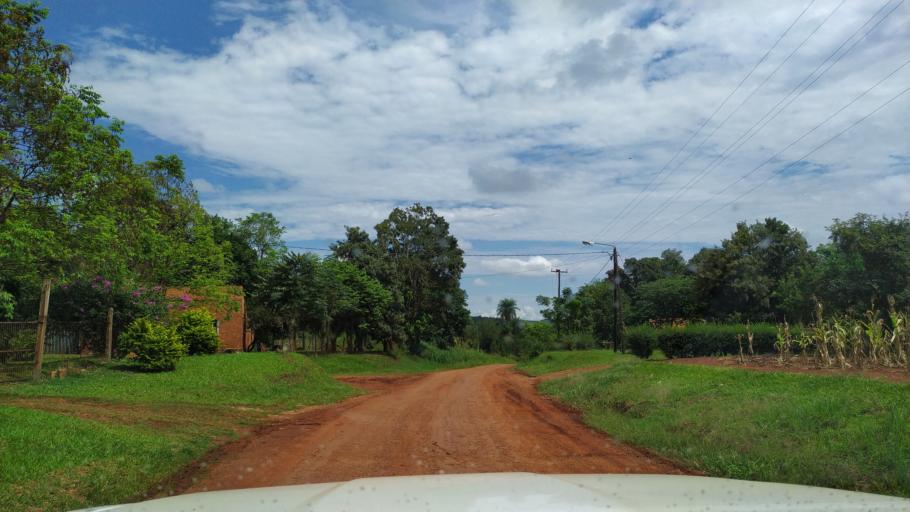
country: AR
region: Misiones
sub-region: Departamento de Eldorado
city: Eldorado
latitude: -26.5158
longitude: -54.5912
